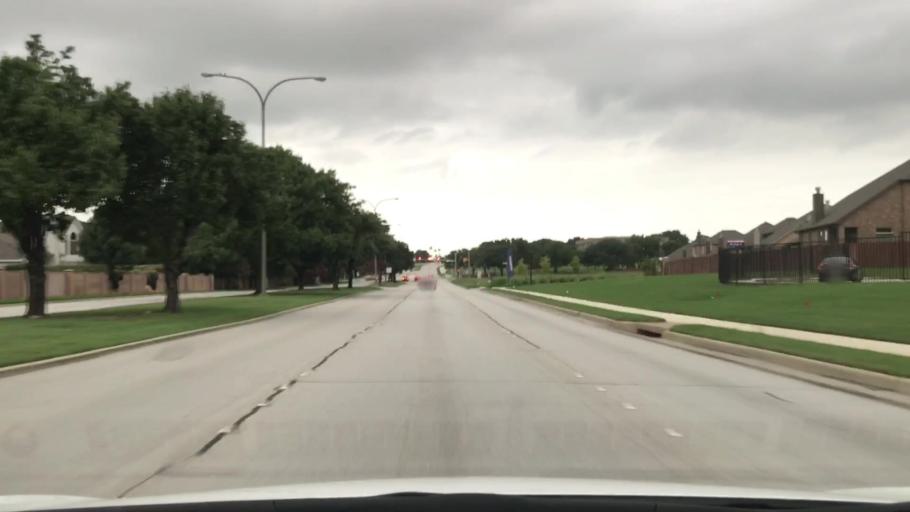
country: US
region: Texas
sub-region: Tarrant County
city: Watauga
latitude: 32.8523
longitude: -97.2901
